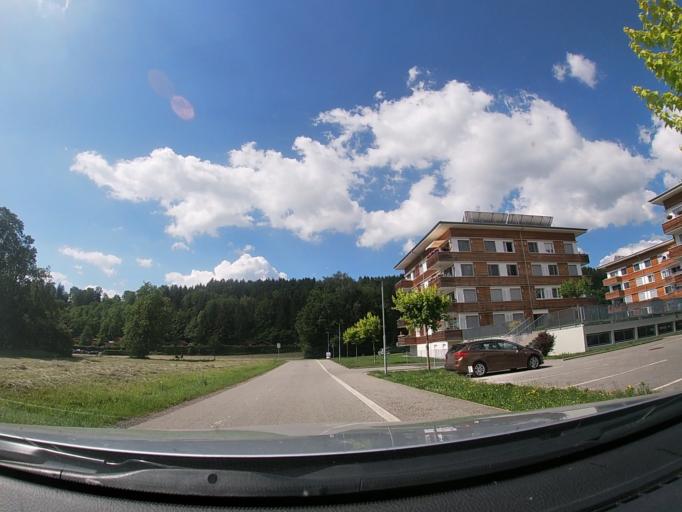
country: AT
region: Styria
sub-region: Politischer Bezirk Leoben
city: Trofaiach
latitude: 47.4214
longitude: 14.9960
